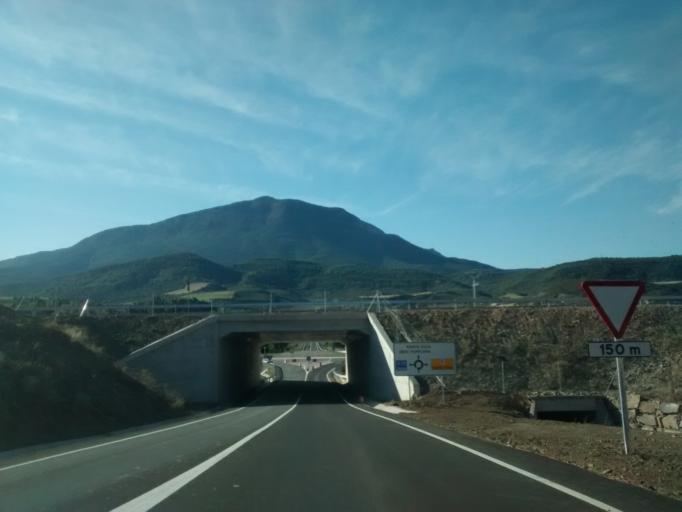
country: ES
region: Aragon
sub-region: Provincia de Huesca
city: Santa Cruz de la Seros
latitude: 42.5657
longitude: -0.7124
